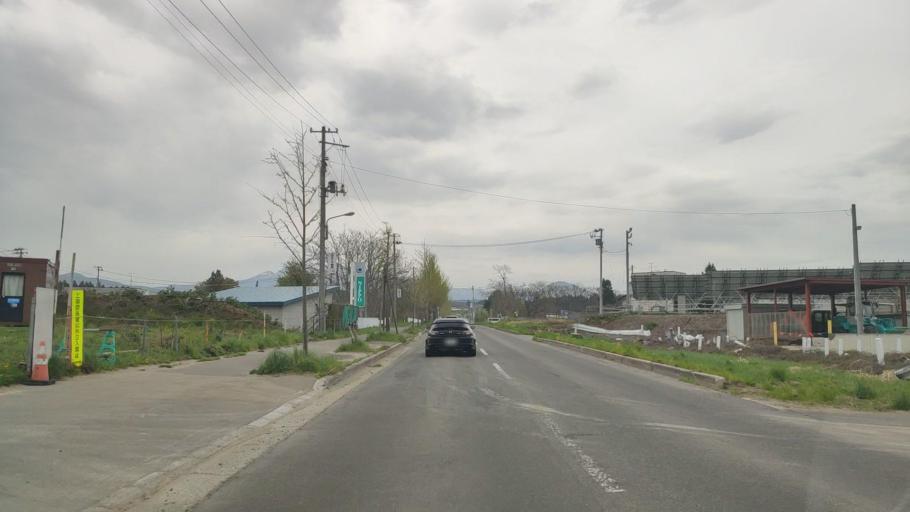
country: JP
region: Aomori
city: Aomori Shi
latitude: 40.7961
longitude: 140.7847
